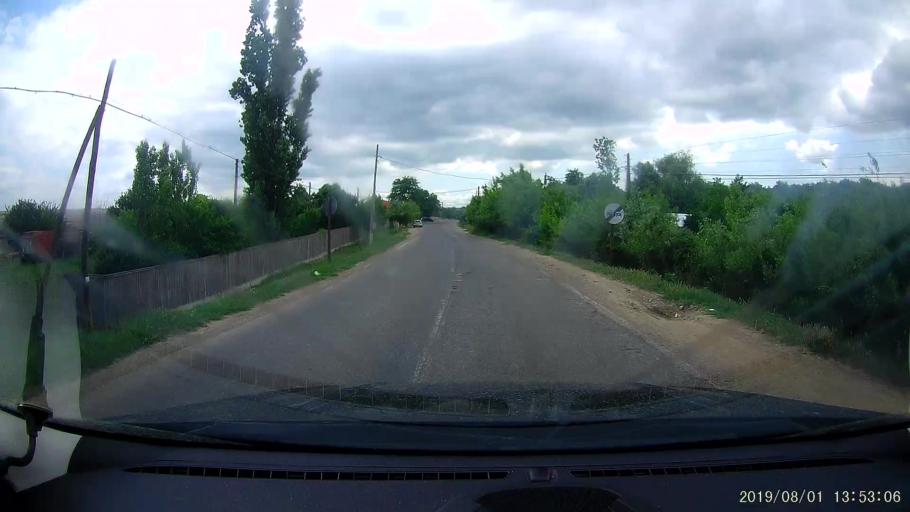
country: RO
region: Galati
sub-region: Comuna Vladesti
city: Vladesti
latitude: 45.8432
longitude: 28.0936
